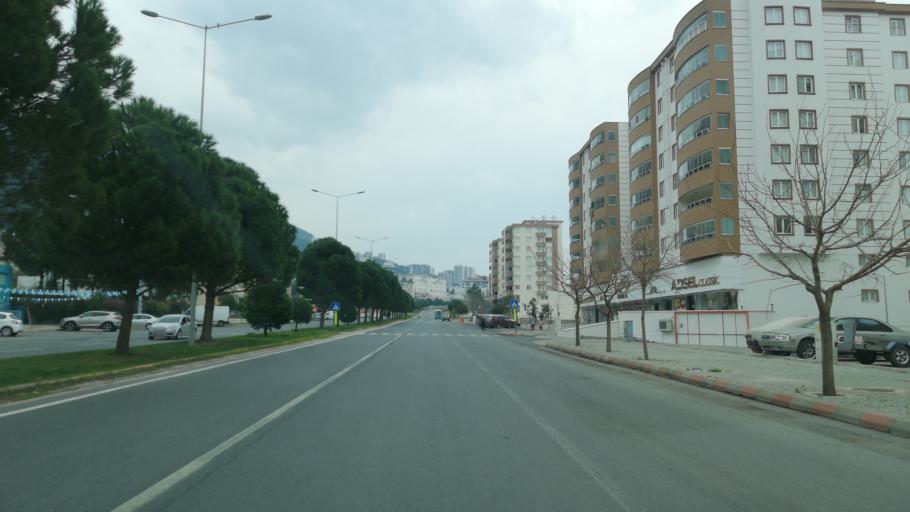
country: TR
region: Kahramanmaras
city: Kahramanmaras
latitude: 37.5999
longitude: 36.8273
